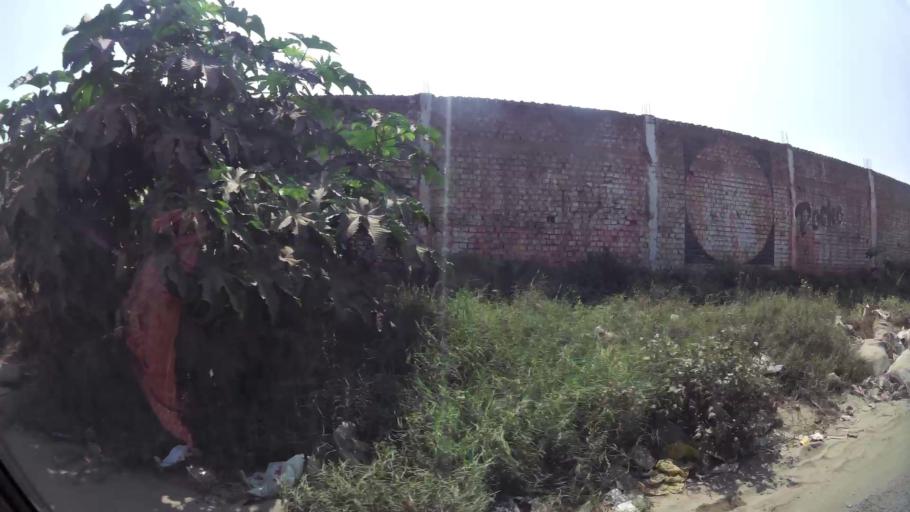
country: PE
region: La Libertad
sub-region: Provincia de Trujillo
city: Buenos Aires
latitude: -8.1292
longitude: -79.0489
